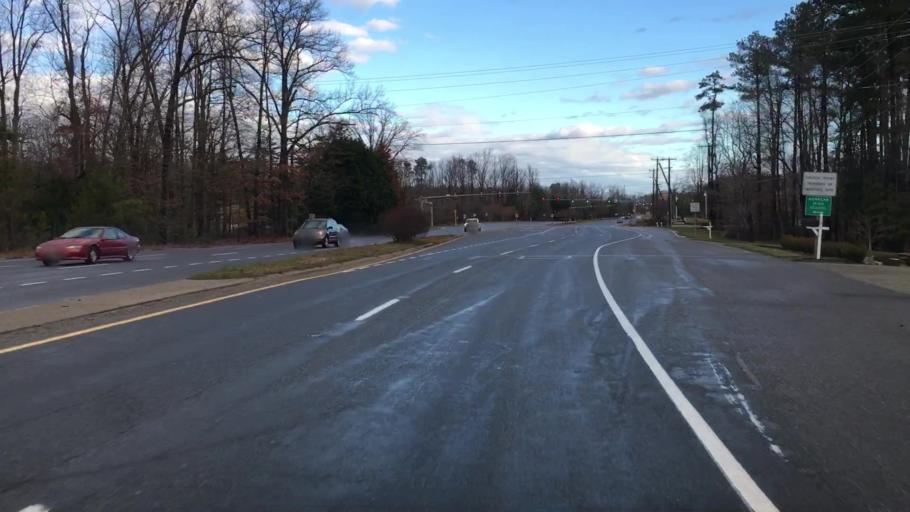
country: US
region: Virginia
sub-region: Chesterfield County
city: Bon Air
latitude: 37.4830
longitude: -77.5980
